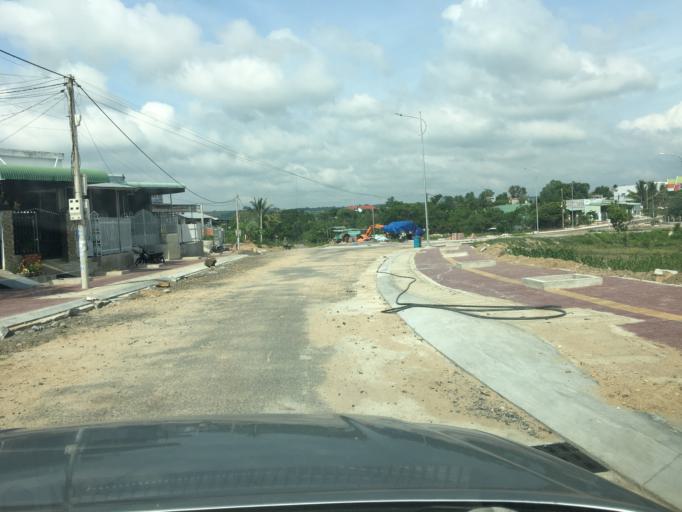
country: VN
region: Gia Lai
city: Kong Chro
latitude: 13.7738
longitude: 108.5276
